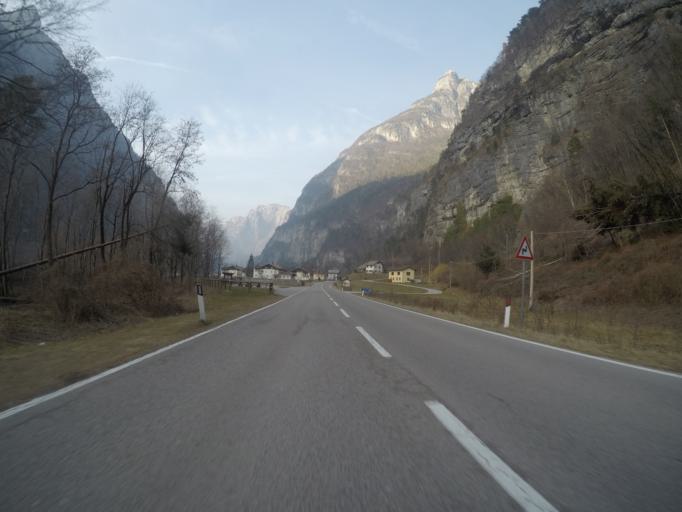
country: IT
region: Veneto
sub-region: Provincia di Belluno
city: Sospirolo
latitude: 46.2130
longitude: 12.1289
